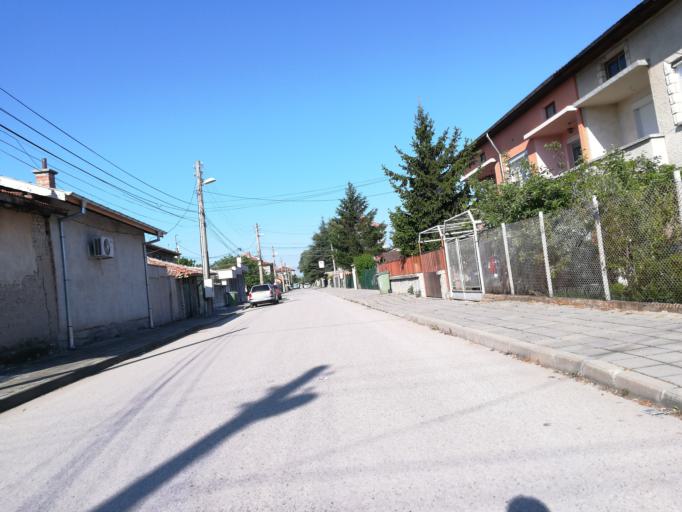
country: BG
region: Stara Zagora
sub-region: Obshtina Chirpan
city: Chirpan
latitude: 42.1031
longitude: 25.2327
